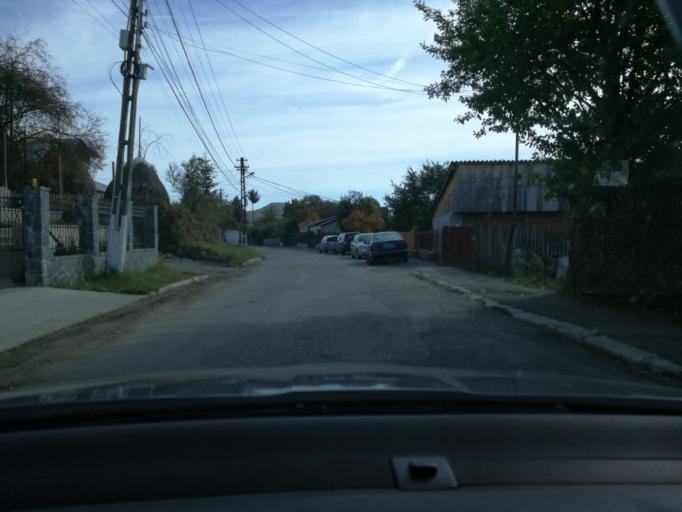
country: RO
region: Prahova
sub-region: Municipiul Campina
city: Campina
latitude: 45.1386
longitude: 25.7425
